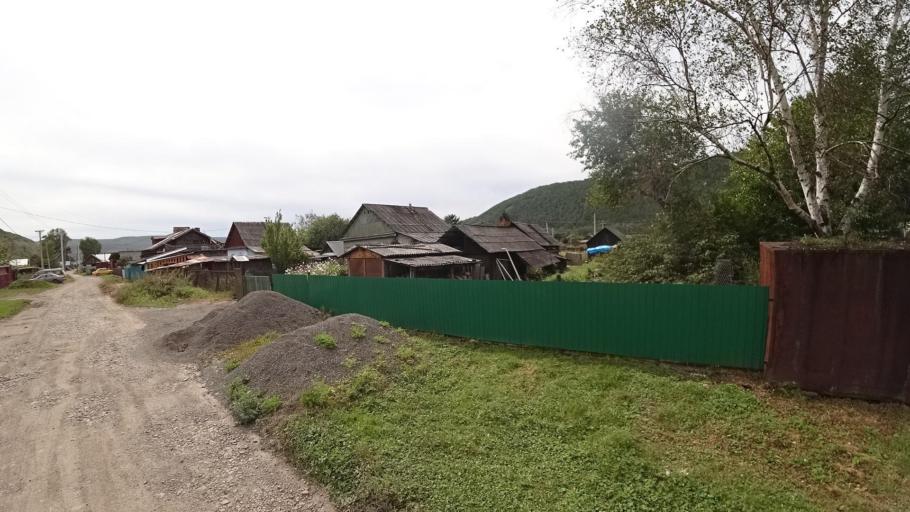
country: RU
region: Jewish Autonomous Oblast
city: Khingansk
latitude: 48.9990
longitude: 131.0543
